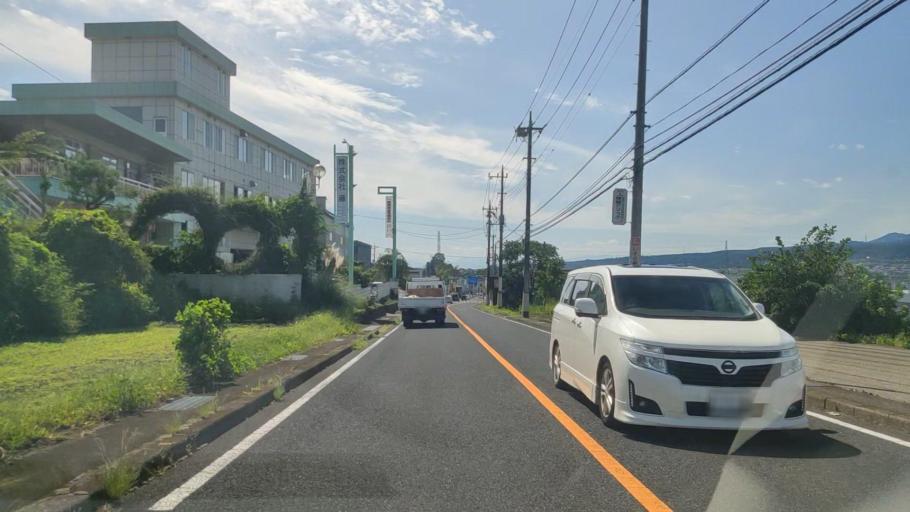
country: JP
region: Gunma
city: Shibukawa
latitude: 36.5229
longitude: 139.0114
